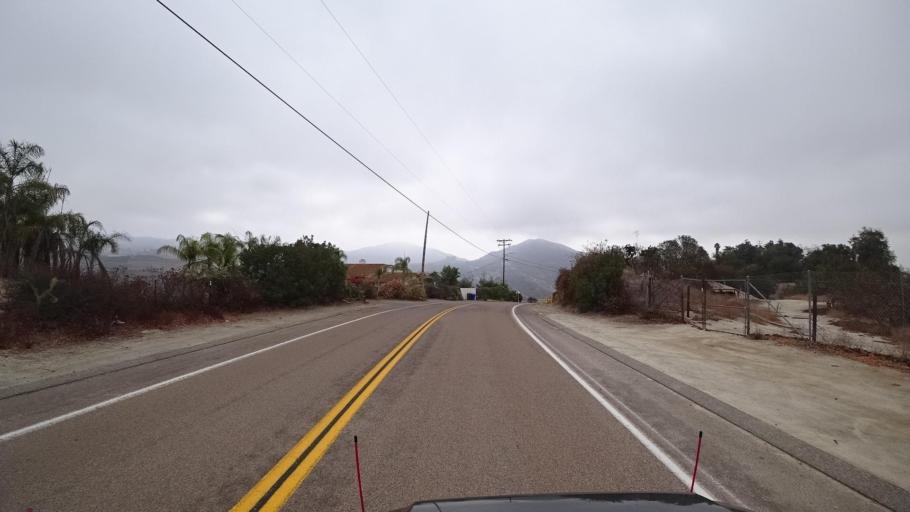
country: US
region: California
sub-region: San Diego County
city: Rainbow
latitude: 33.3840
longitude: -117.1702
